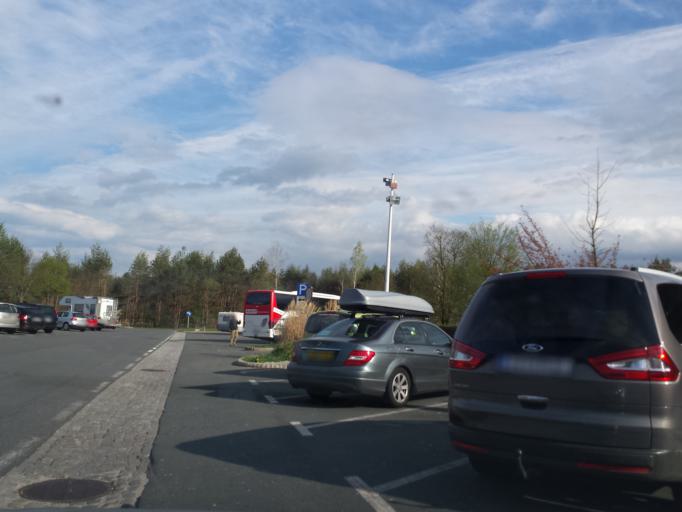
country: AT
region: Styria
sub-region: Politischer Bezirk Graz-Umgebung
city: Unterpremstatten
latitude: 46.9587
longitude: 15.3818
